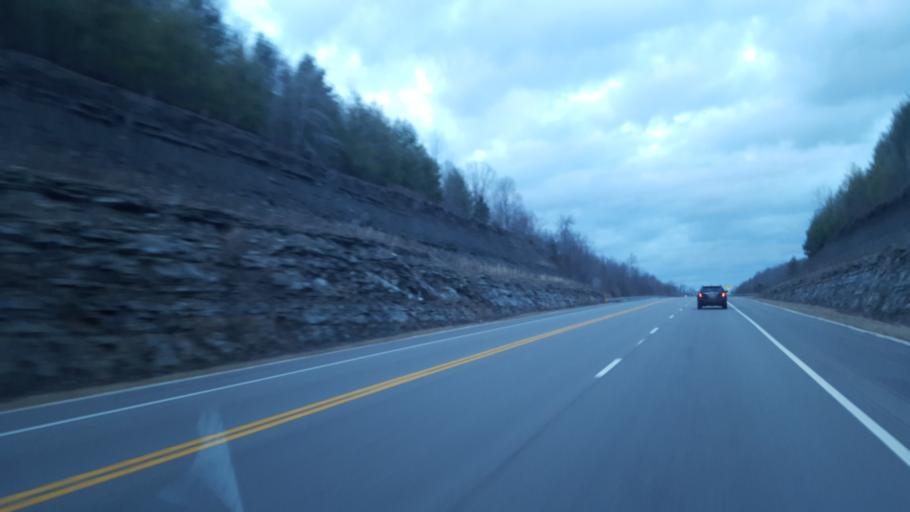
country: US
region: Kentucky
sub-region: Lewis County
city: Vanceburg
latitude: 38.5798
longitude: -83.2731
